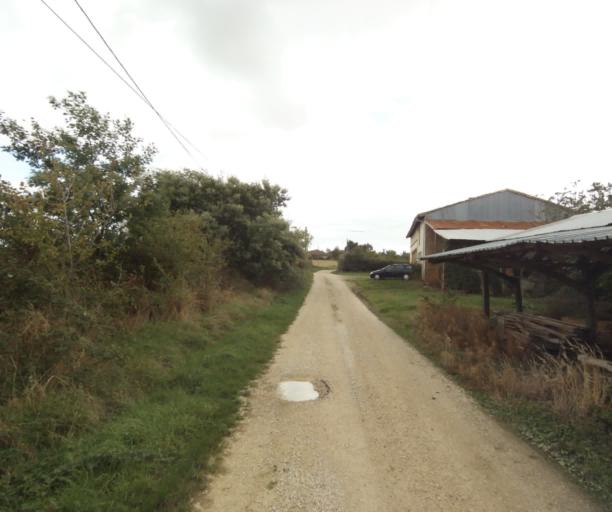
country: FR
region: Midi-Pyrenees
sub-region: Departement du Tarn-et-Garonne
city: Beaumont-de-Lomagne
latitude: 43.8993
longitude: 1.0892
